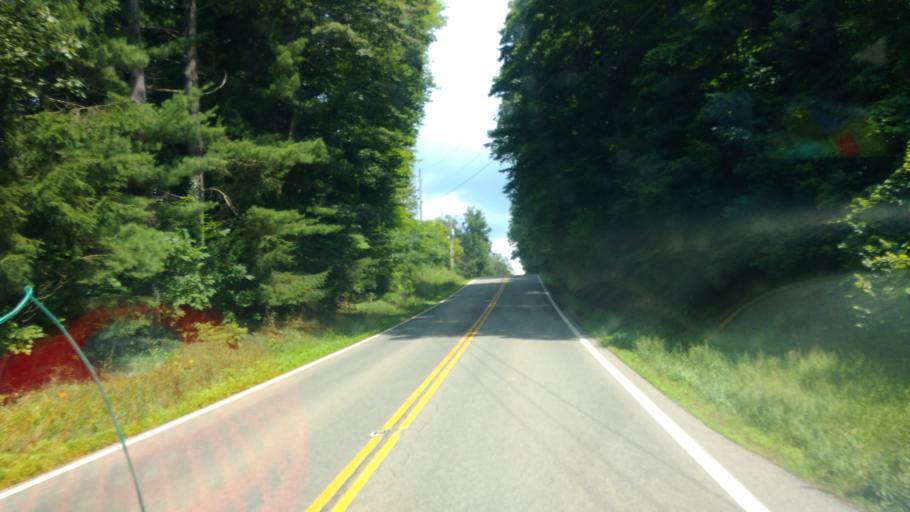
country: US
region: Ohio
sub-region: Ashland County
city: Loudonville
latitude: 40.7225
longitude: -82.3179
